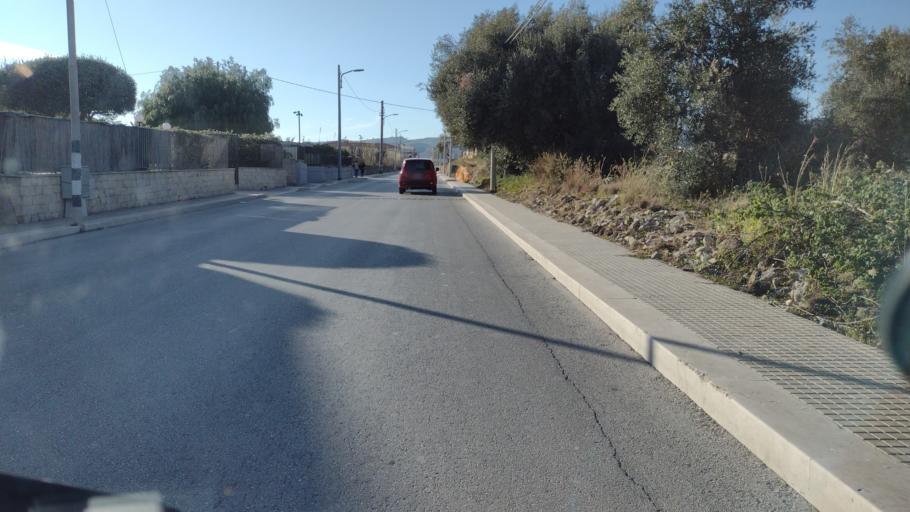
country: IT
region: Sicily
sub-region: Provincia di Siracusa
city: Avola
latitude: 36.9012
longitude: 15.1415
